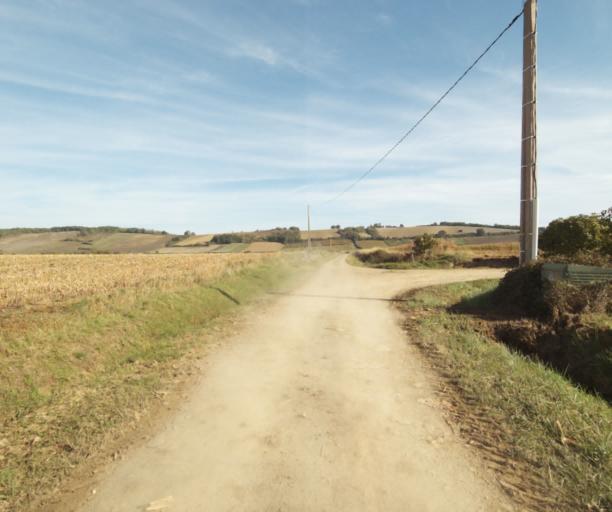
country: FR
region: Midi-Pyrenees
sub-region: Departement du Tarn-et-Garonne
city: Orgueil
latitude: 43.9172
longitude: 1.4309
